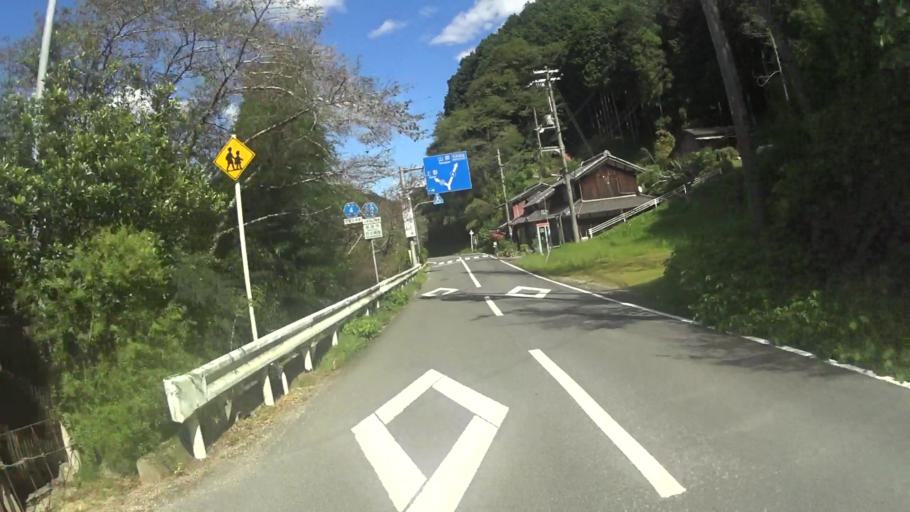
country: JP
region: Mie
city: Nabari
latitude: 34.7048
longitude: 136.0292
